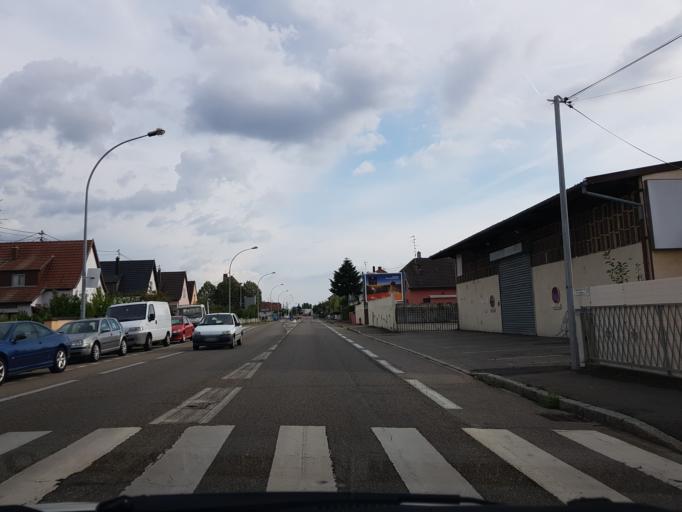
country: FR
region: Alsace
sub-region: Departement du Haut-Rhin
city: Wittenheim
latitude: 47.8204
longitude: 7.3397
